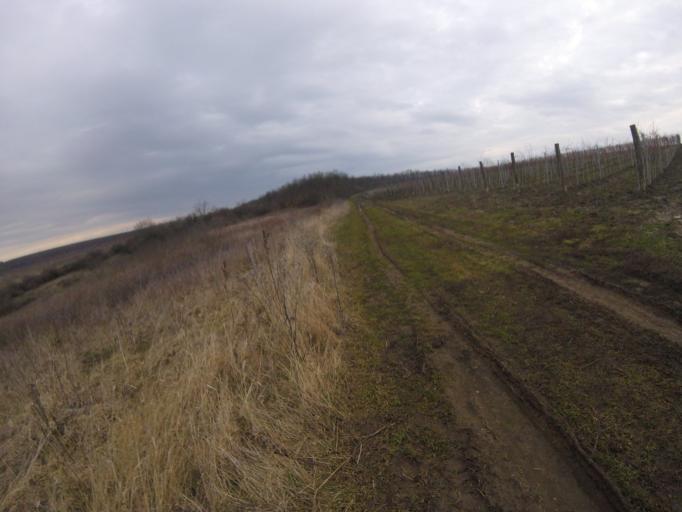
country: HU
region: Heves
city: Kerecsend
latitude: 47.8312
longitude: 20.3459
